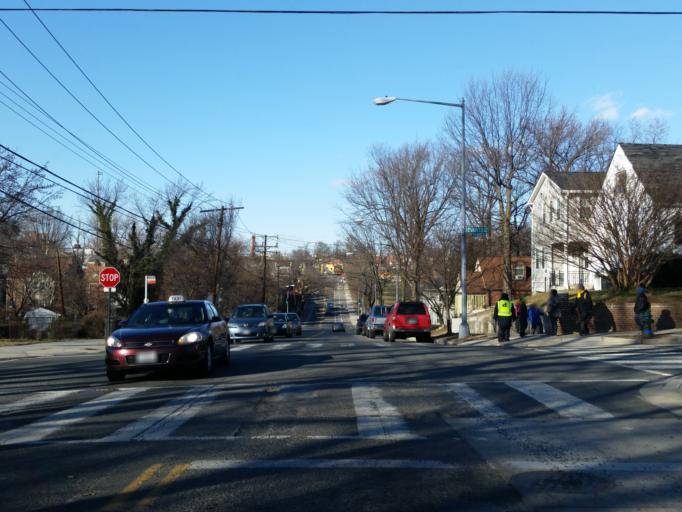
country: US
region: Maryland
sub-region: Prince George's County
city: Mount Rainier
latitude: 38.9244
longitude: -76.9790
